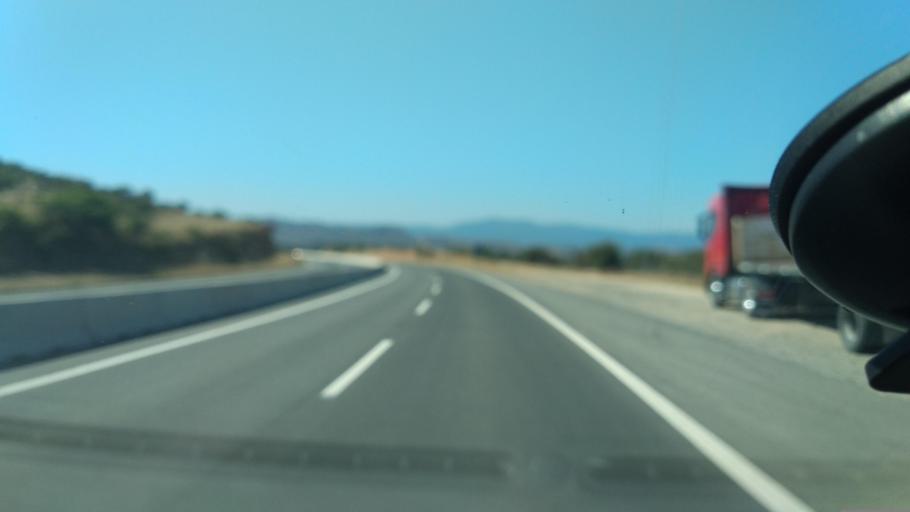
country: CL
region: Valparaiso
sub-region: Provincia de Marga Marga
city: Villa Alemana
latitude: -33.0023
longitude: -71.3284
